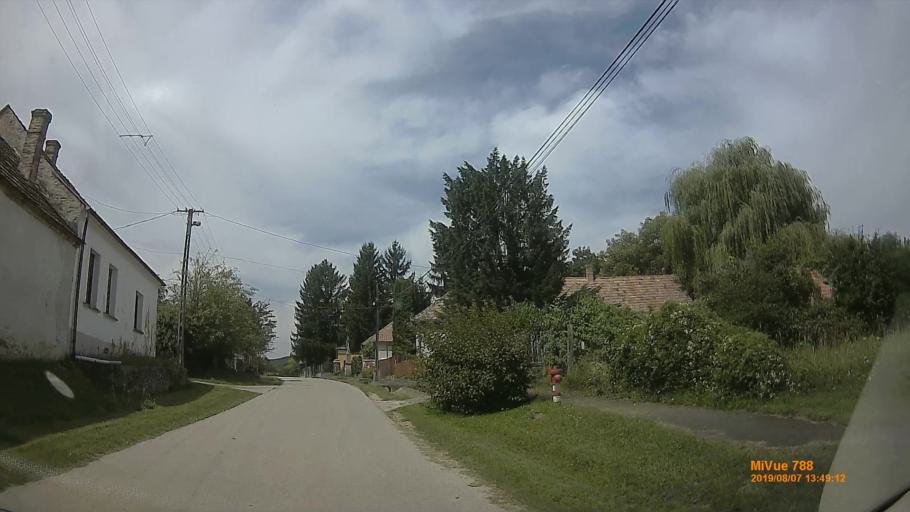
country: HU
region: Zala
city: Cserszegtomaj
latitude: 46.8870
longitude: 17.1932
